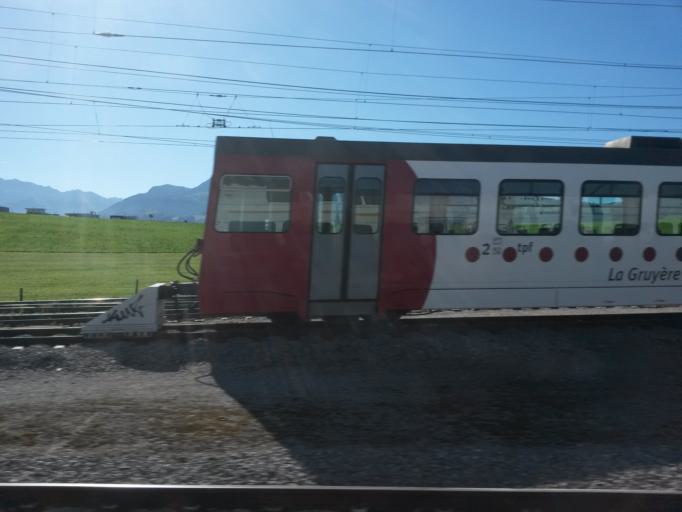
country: CH
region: Fribourg
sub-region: Gruyere District
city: Bulle
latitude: 46.6217
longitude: 7.0447
